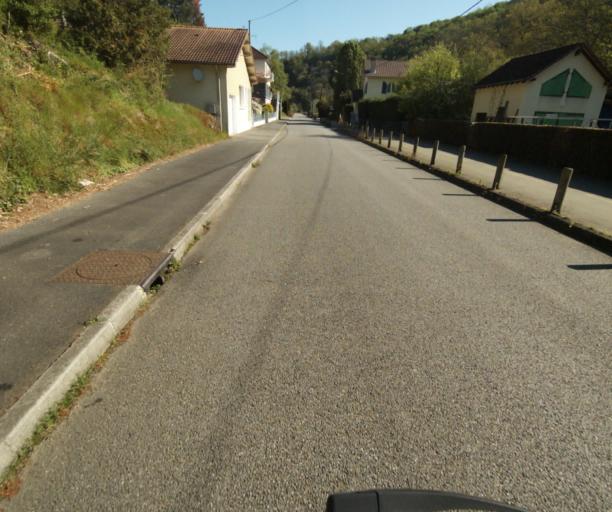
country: FR
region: Limousin
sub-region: Departement de la Correze
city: Tulle
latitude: 45.2799
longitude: 1.7855
